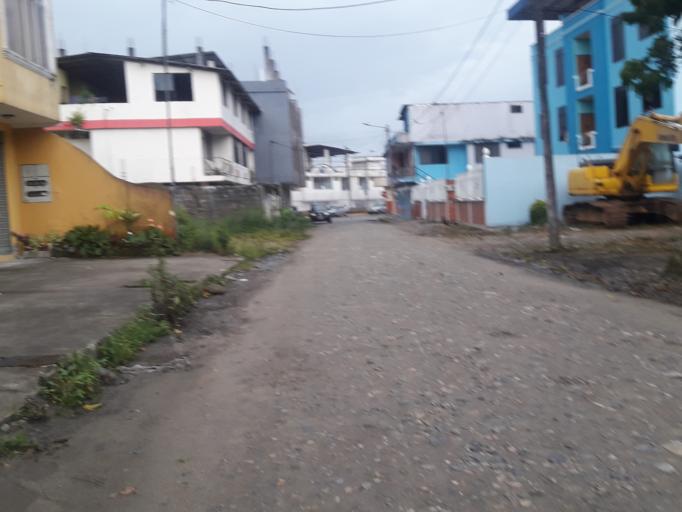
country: EC
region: Napo
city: Tena
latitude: -1.0058
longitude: -77.8113
